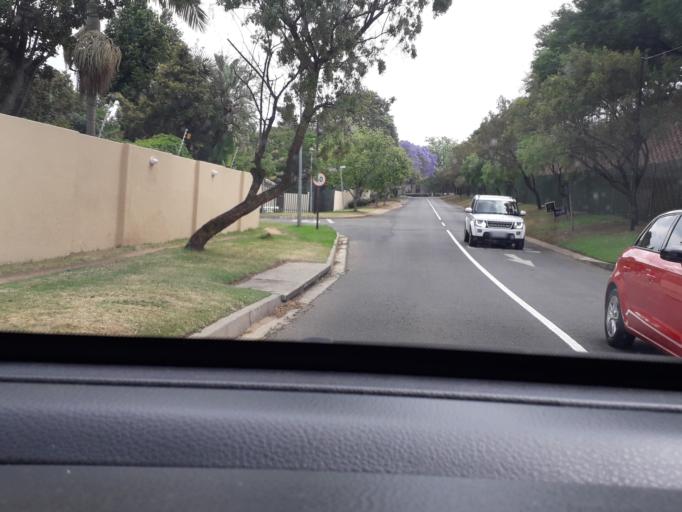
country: ZA
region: Gauteng
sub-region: City of Johannesburg Metropolitan Municipality
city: Modderfontein
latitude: -26.0820
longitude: 28.0579
